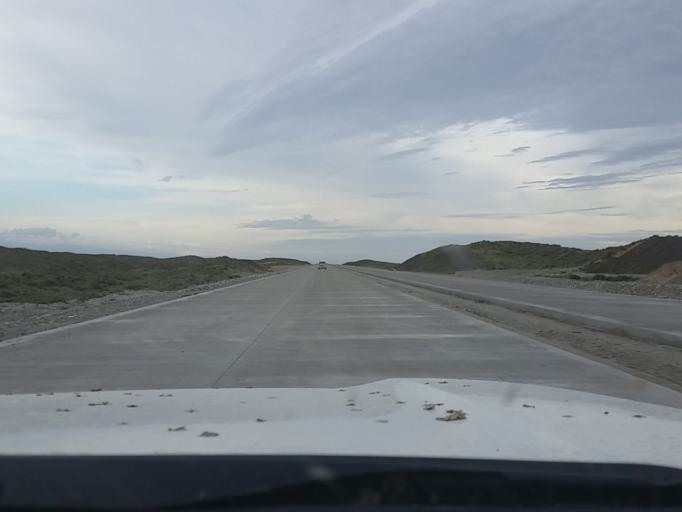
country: KZ
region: Almaty Oblysy
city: Zharkent
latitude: 44.1745
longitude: 80.3108
